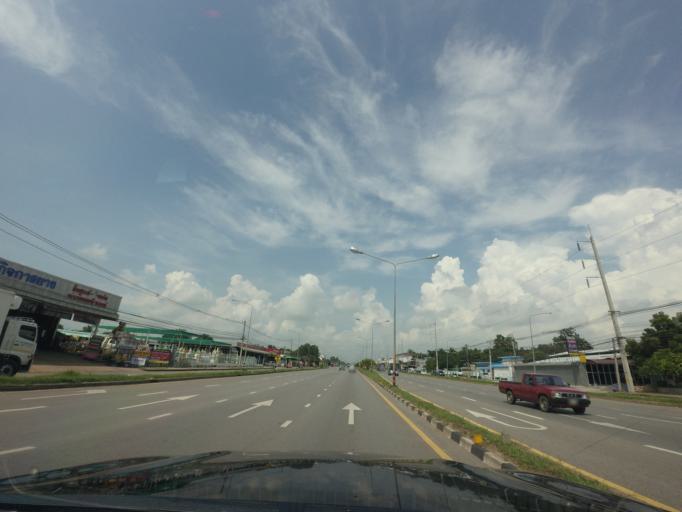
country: TH
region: Khon Kaen
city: Ban Fang
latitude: 16.4501
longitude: 102.7198
